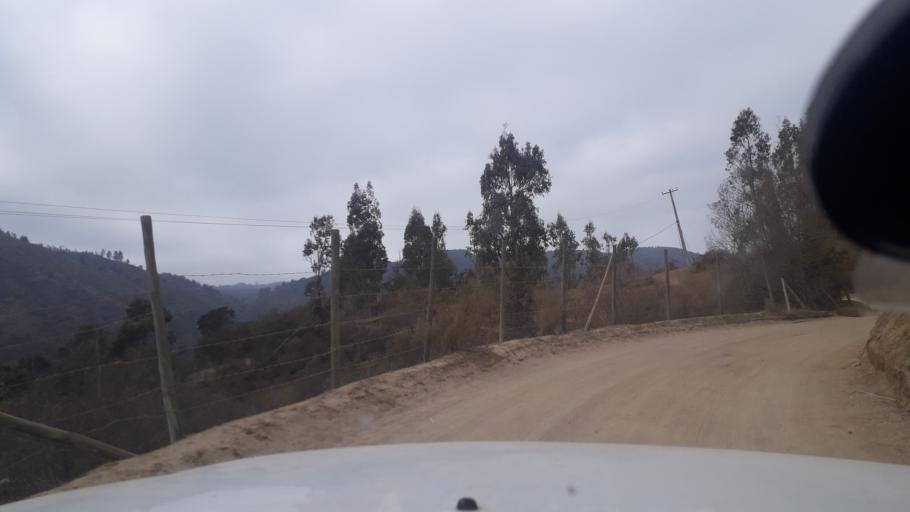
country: CL
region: Valparaiso
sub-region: Provincia de Valparaiso
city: Valparaiso
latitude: -33.1156
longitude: -71.6491
